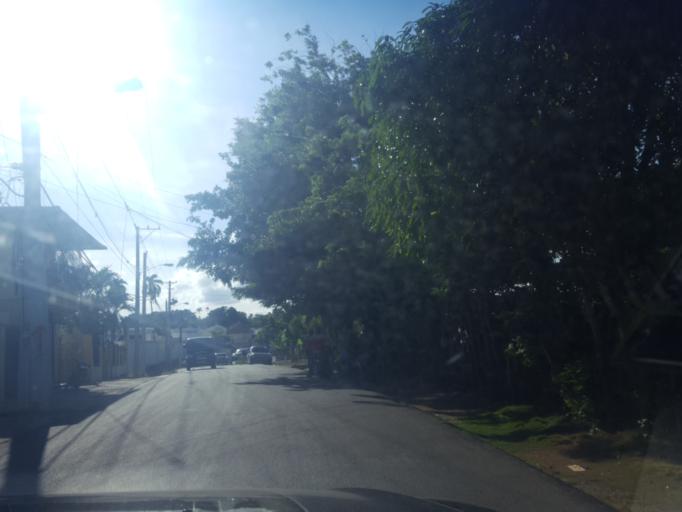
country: DO
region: La Vega
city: Rio Verde Arriba
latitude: 19.3453
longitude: -70.6213
